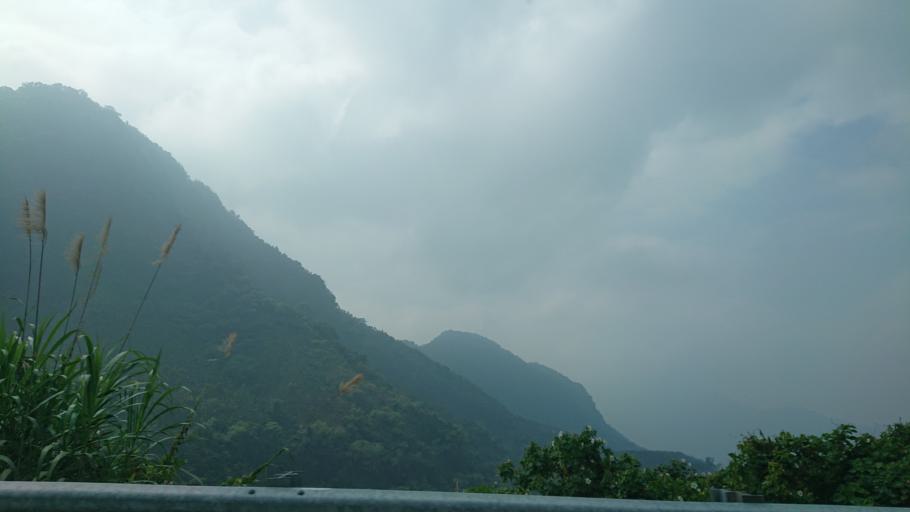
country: TW
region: Taiwan
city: Lugu
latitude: 23.5992
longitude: 120.6896
